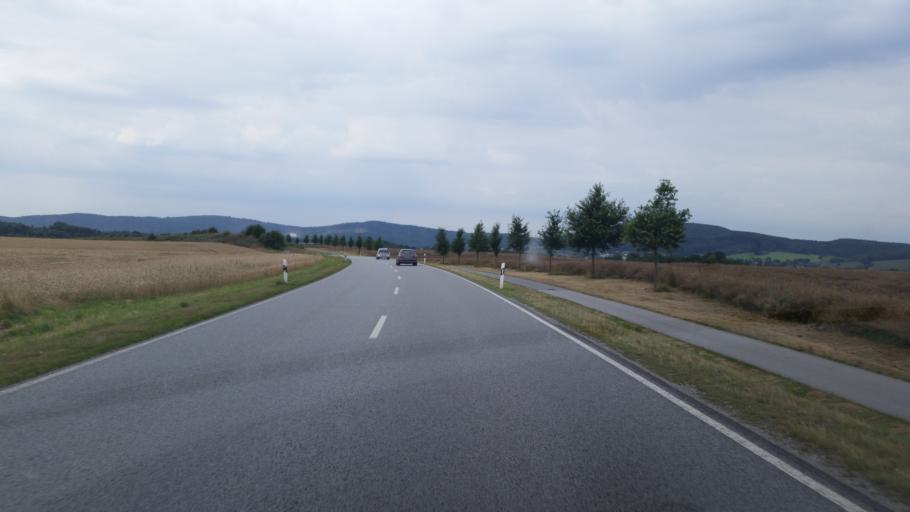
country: DE
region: Saxony
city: Elstra
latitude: 51.2317
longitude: 14.1501
